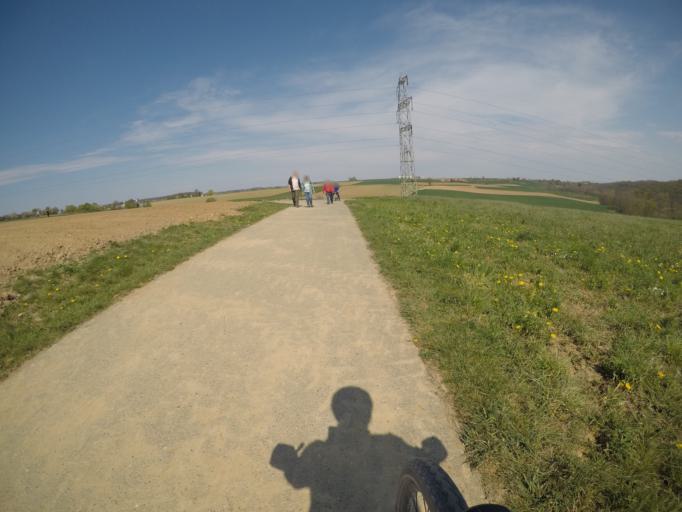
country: DE
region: Baden-Wuerttemberg
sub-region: Regierungsbezirk Stuttgart
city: Hemmingen
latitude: 48.8457
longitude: 9.0454
